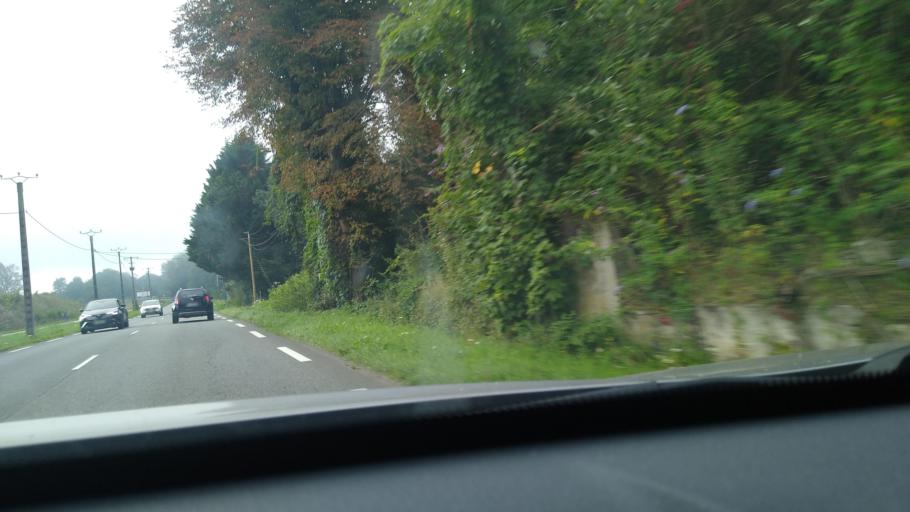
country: FR
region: Midi-Pyrenees
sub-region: Departement de la Haute-Garonne
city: Salies-du-Salat
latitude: 43.0752
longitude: 0.9614
